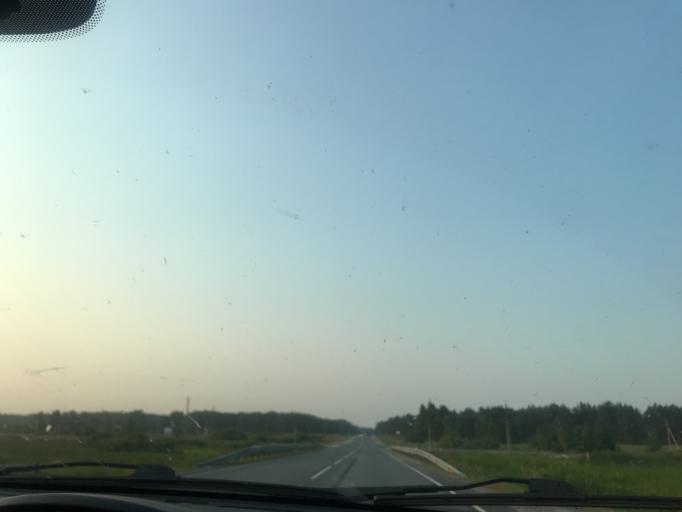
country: RU
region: Novosibirsk
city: Dorogino
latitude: 54.3737
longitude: 83.3045
